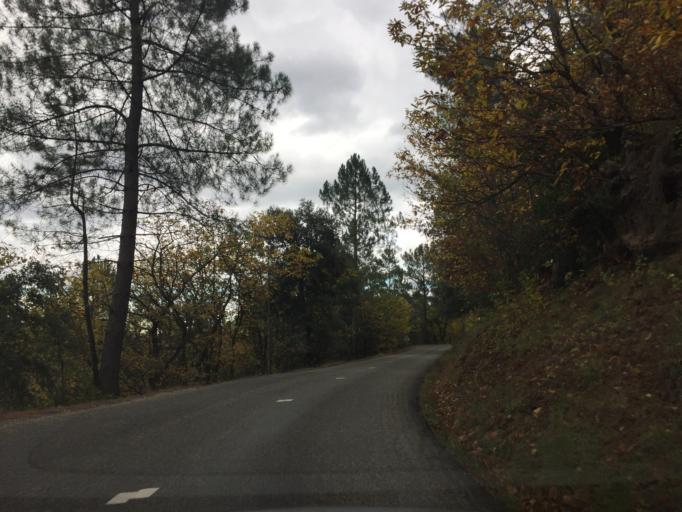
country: FR
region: Rhone-Alpes
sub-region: Departement de l'Ardeche
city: Les Vans
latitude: 44.4132
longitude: 4.0966
